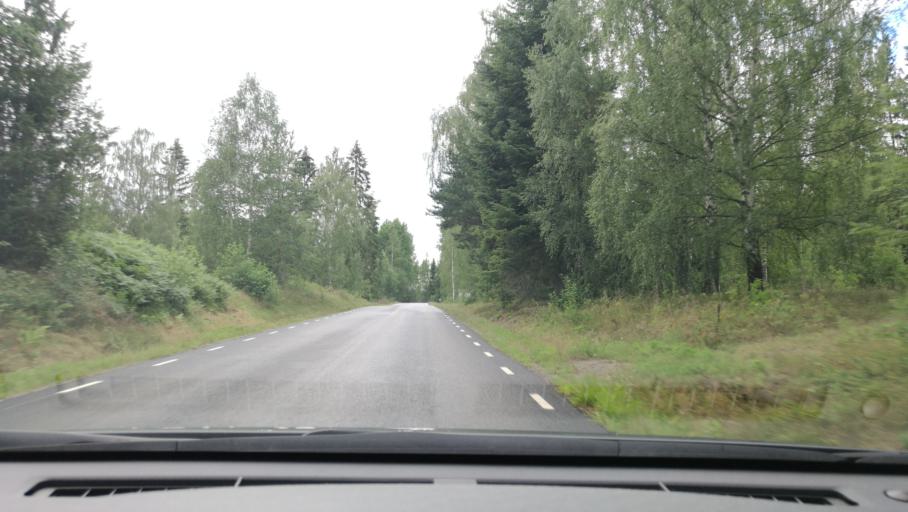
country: SE
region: OEstergoetland
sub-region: Norrkopings Kommun
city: Svartinge
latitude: 58.8235
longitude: 15.9903
